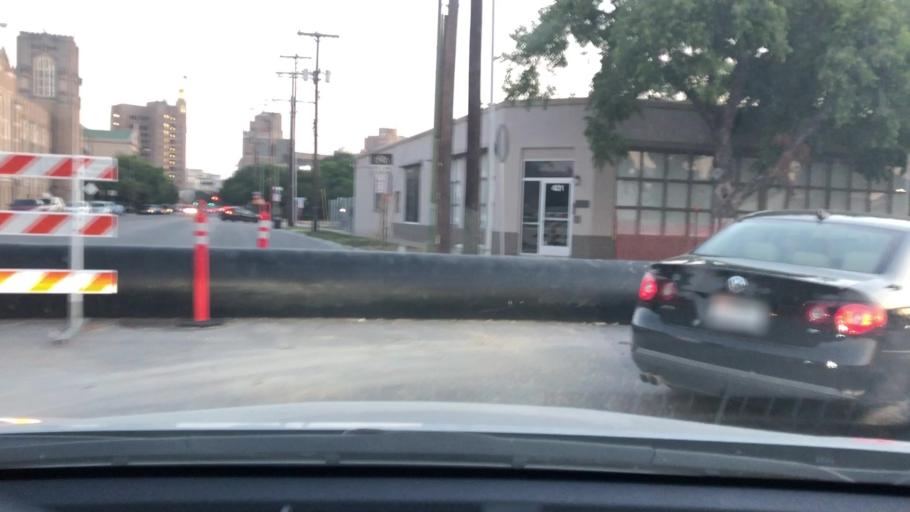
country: US
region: Texas
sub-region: Bexar County
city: San Antonio
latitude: 29.4297
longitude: -98.4826
